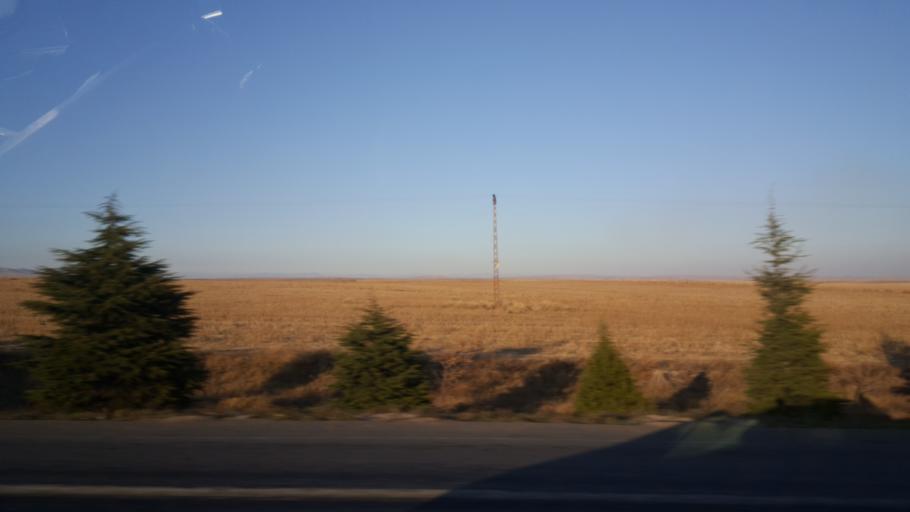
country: TR
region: Eskisehir
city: Mahmudiye
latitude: 39.5832
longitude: 30.9044
